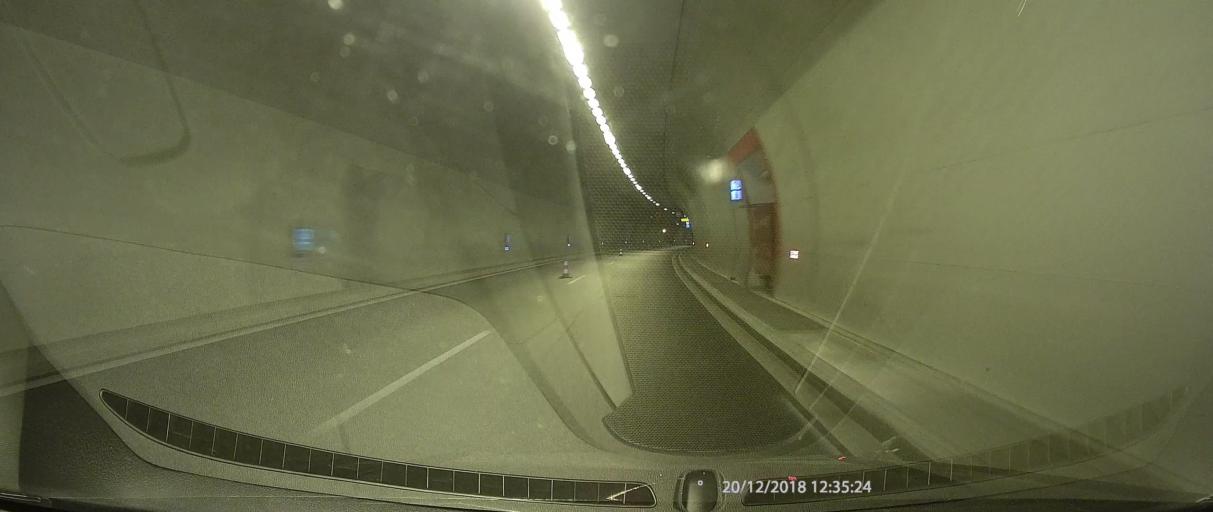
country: GR
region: West Greece
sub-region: Nomos Aitolias kai Akarnanias
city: Antirrio
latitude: 38.3542
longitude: 21.6964
